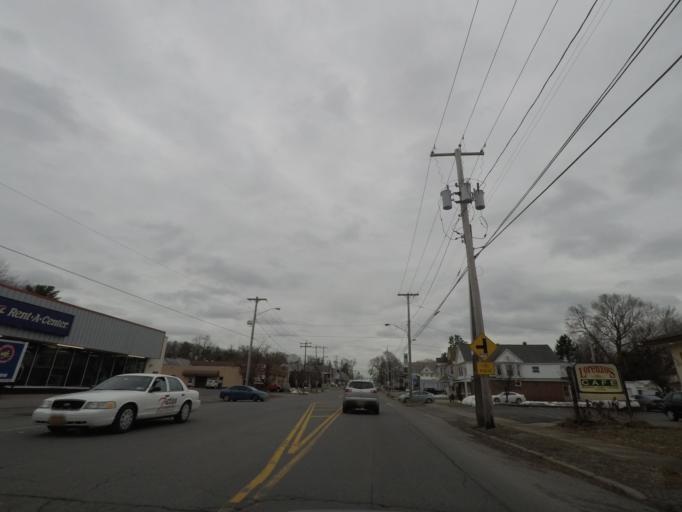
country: US
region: New York
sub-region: Schenectady County
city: Schenectady
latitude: 42.7917
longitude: -73.9168
